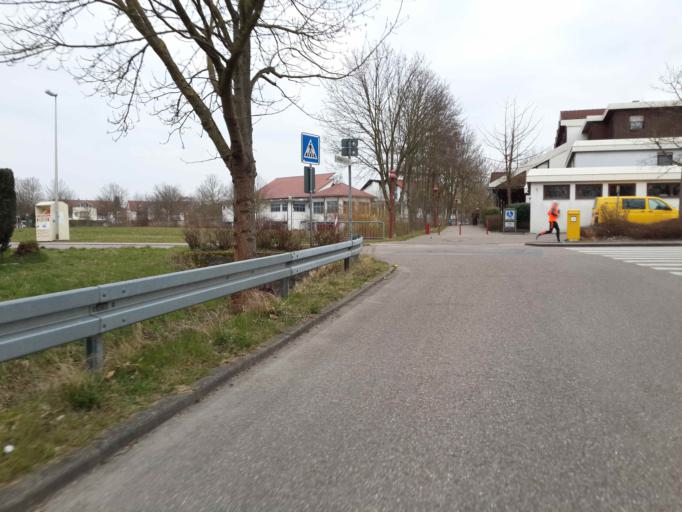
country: DE
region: Baden-Wuerttemberg
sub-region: Regierungsbezirk Stuttgart
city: Leingarten
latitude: 49.1449
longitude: 9.1097
